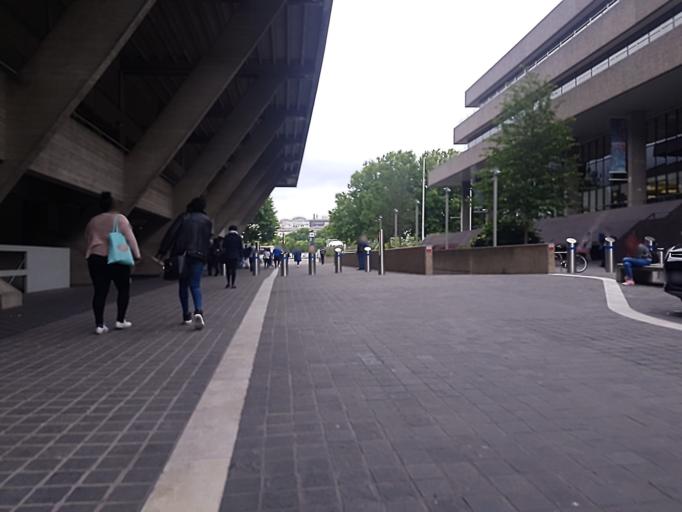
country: GB
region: England
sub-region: Greater London
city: City of Westminster
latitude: 51.5071
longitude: -0.1132
